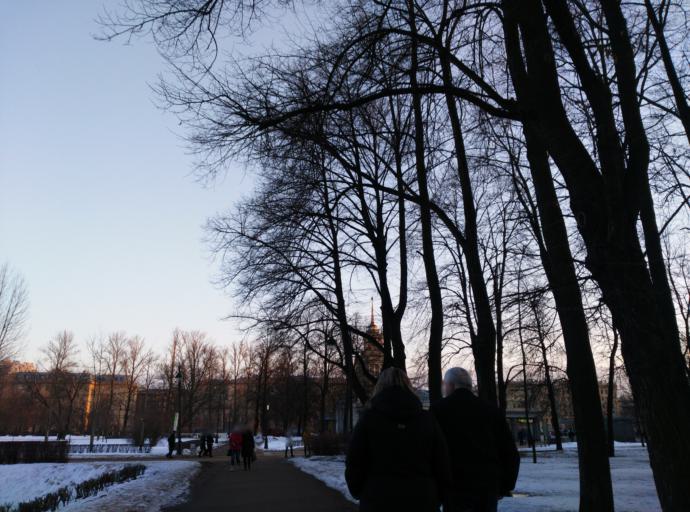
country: RU
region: St.-Petersburg
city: Kupchino
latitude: 59.8672
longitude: 30.3223
